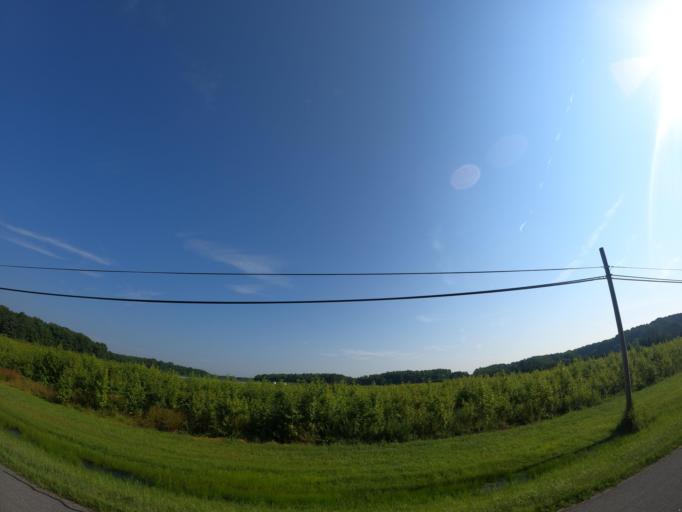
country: US
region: Delaware
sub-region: Sussex County
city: Georgetown
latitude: 38.6979
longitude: -75.4325
